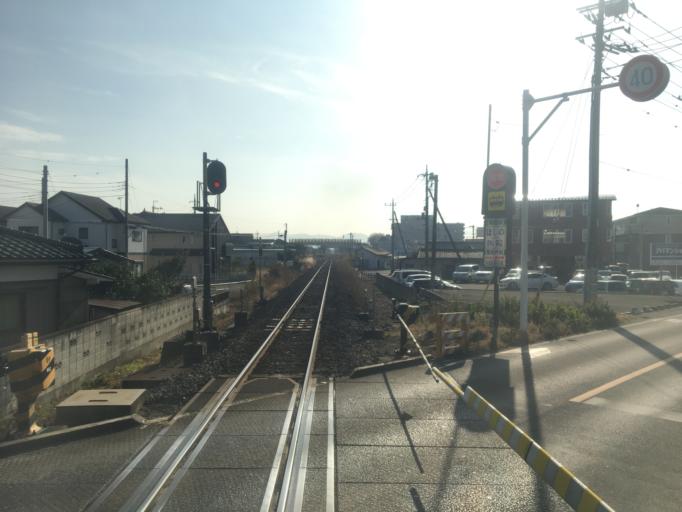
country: JP
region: Gunma
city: Fujioka
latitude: 36.2534
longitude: 139.0835
